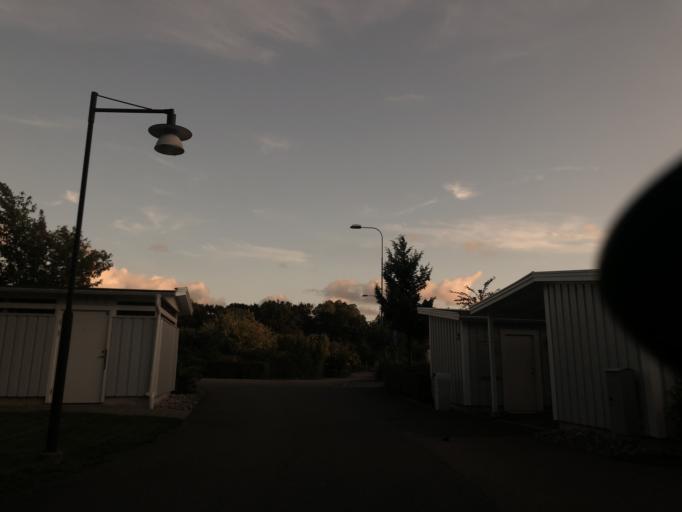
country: SE
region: Vaestra Goetaland
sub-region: Goteborg
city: Goeteborg
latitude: 57.7594
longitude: 11.9307
